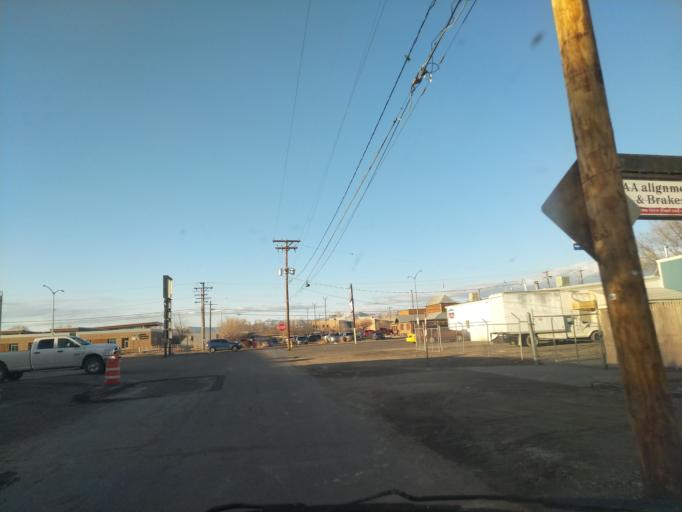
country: US
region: Colorado
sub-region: Mesa County
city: Fruitvale
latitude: 39.0766
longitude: -108.5210
